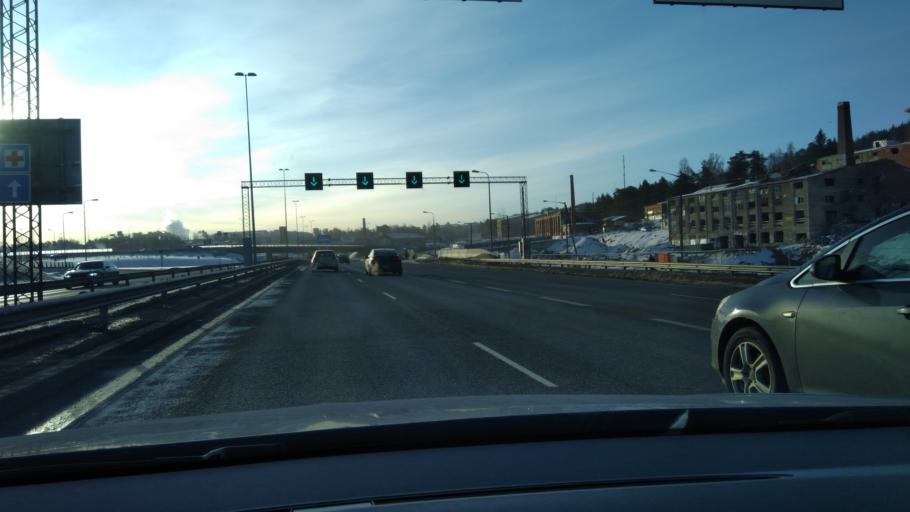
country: FI
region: Pirkanmaa
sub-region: Tampere
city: Tampere
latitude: 61.5047
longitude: 23.7198
